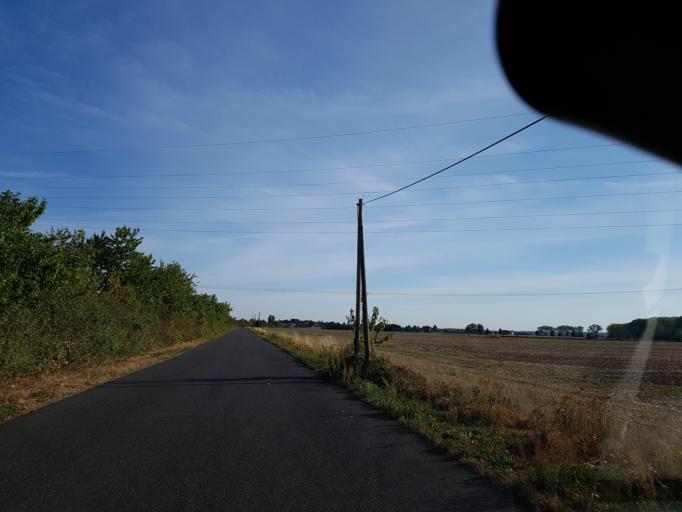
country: DE
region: Saxony
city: Nauwalde
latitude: 51.4506
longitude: 13.4205
